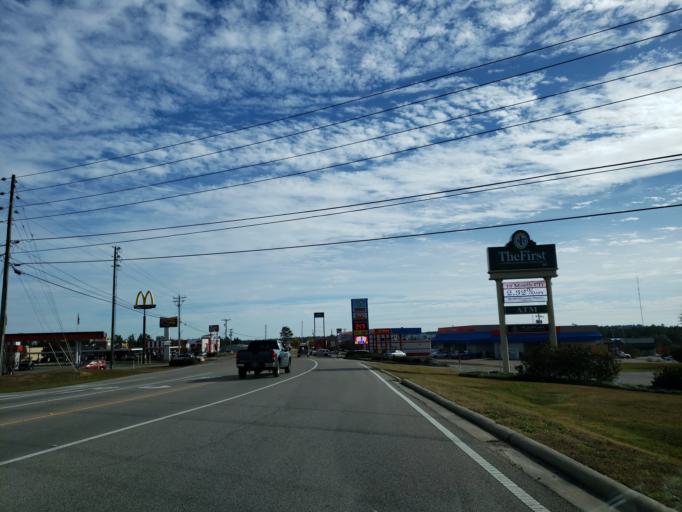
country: US
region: Mississippi
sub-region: Lamar County
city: West Hattiesburg
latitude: 31.3170
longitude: -89.4130
